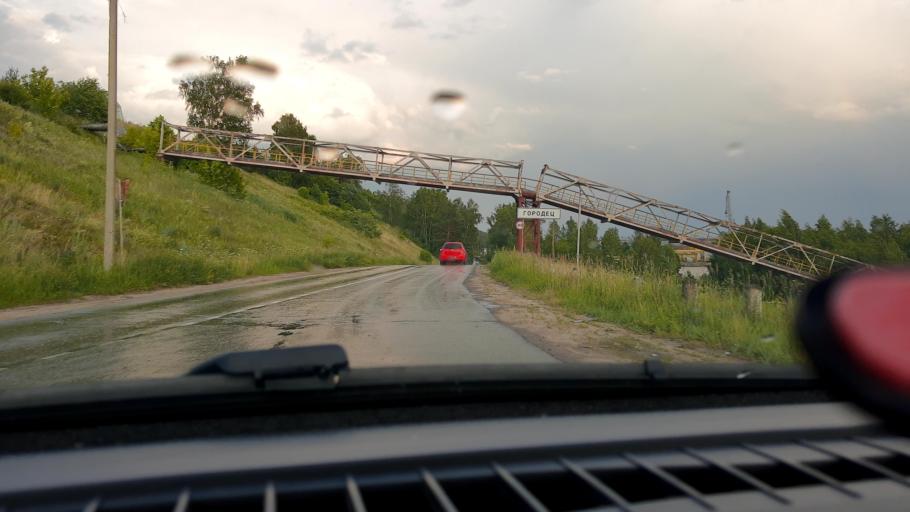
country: RU
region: Nizjnij Novgorod
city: Gorodets
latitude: 56.6847
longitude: 43.4283
